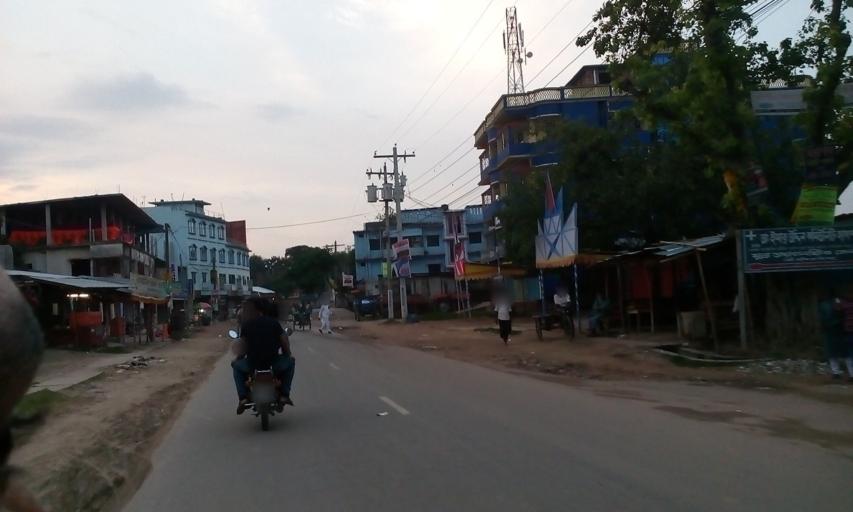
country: IN
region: West Bengal
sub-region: Dakshin Dinajpur
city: Balurghat
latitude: 25.3853
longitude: 88.9881
